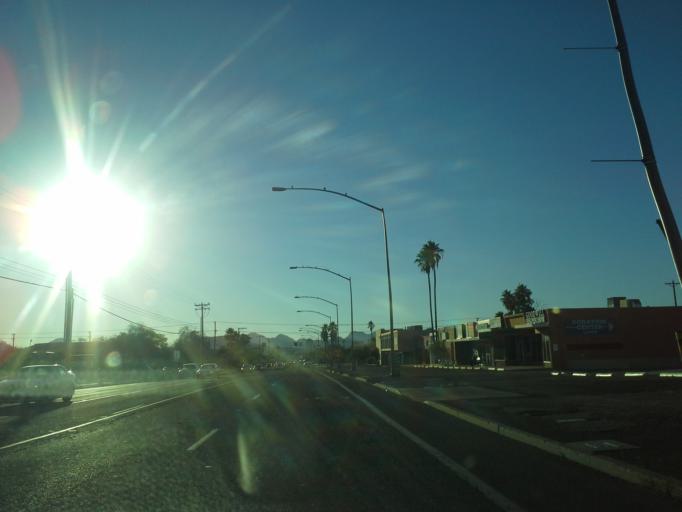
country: US
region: Arizona
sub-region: Pima County
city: Tucson
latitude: 32.2216
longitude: -110.9376
